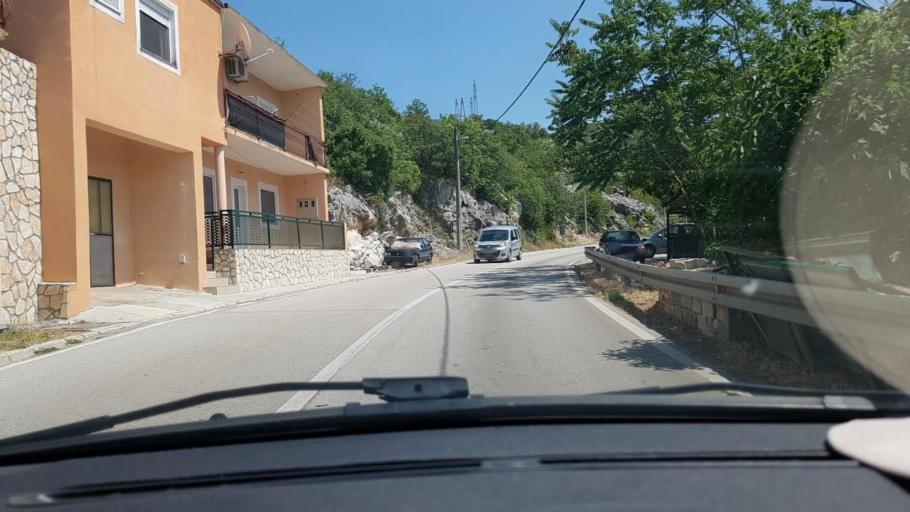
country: HR
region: Splitsko-Dalmatinska
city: Vrgorac
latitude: 43.2008
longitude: 17.3761
